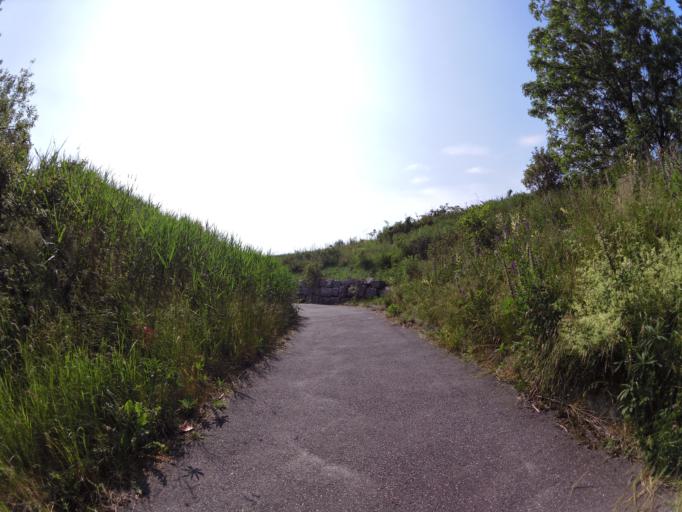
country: NO
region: Ostfold
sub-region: Sarpsborg
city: Sarpsborg
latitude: 59.2613
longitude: 11.1128
